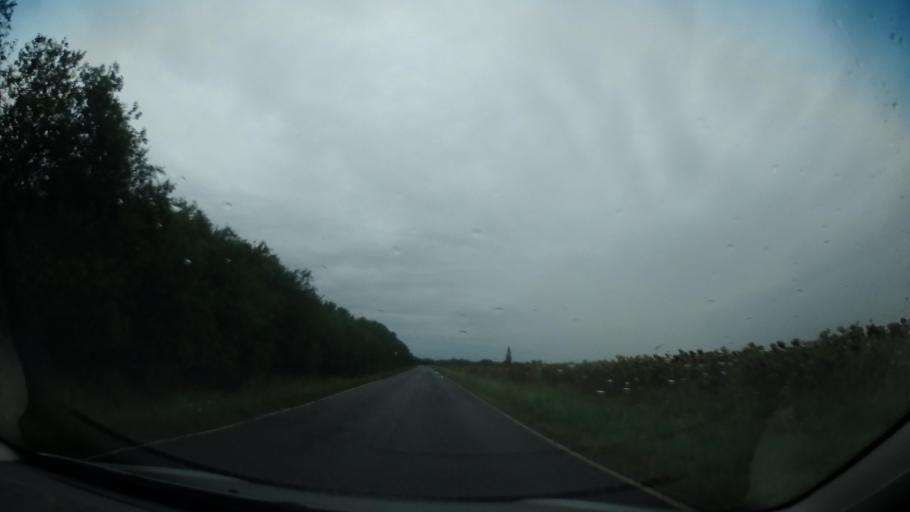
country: CZ
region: Central Bohemia
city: Loucen
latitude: 50.2611
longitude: 15.0240
